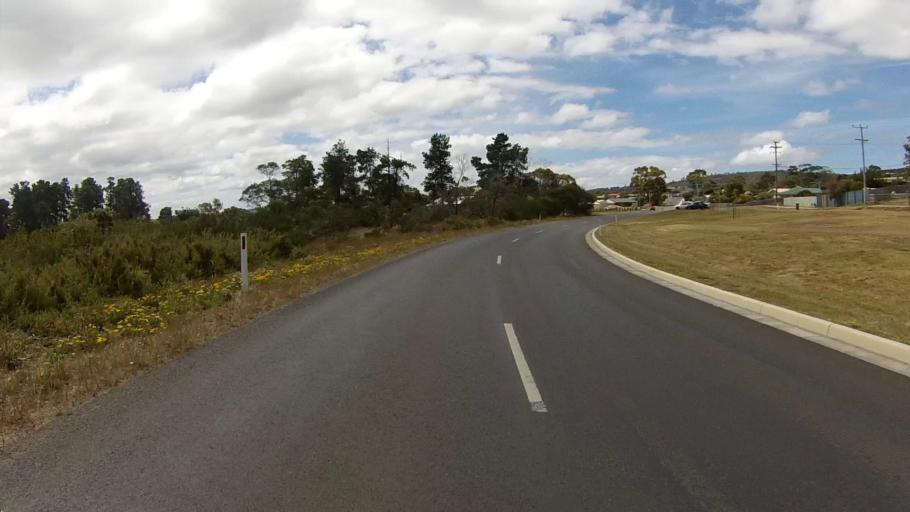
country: AU
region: Tasmania
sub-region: Sorell
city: Sorell
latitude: -42.8602
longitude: 147.6127
